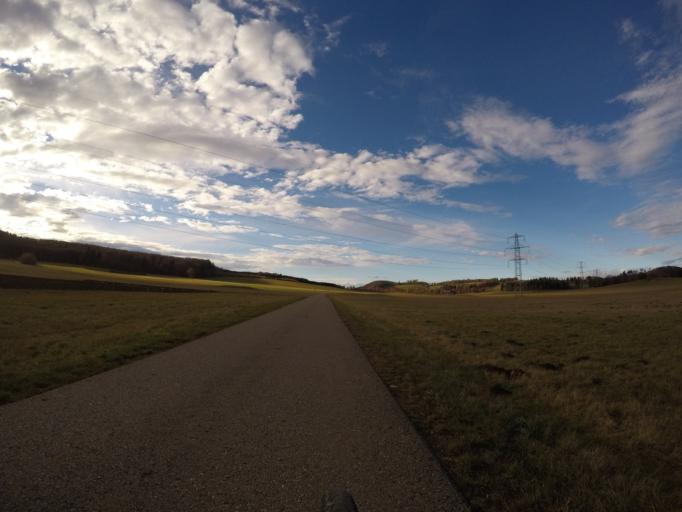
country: DE
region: Baden-Wuerttemberg
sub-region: Tuebingen Region
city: Sankt Johann
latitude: 48.4674
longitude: 9.3151
